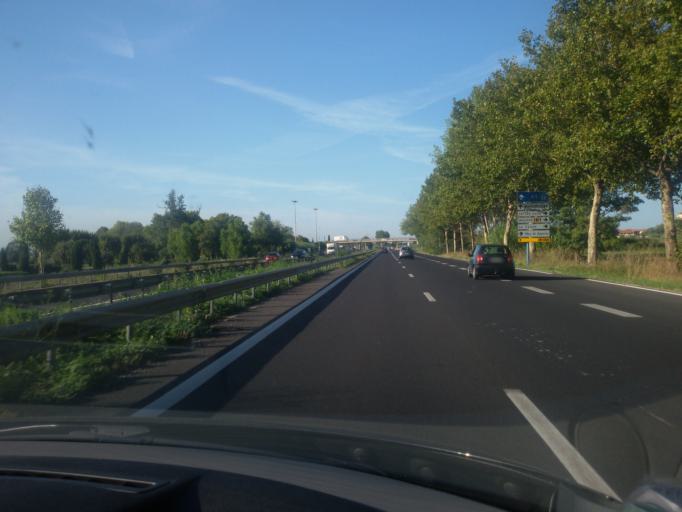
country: FR
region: Languedoc-Roussillon
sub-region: Departement de l'Herault
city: Lattes
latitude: 43.5681
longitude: 3.8954
